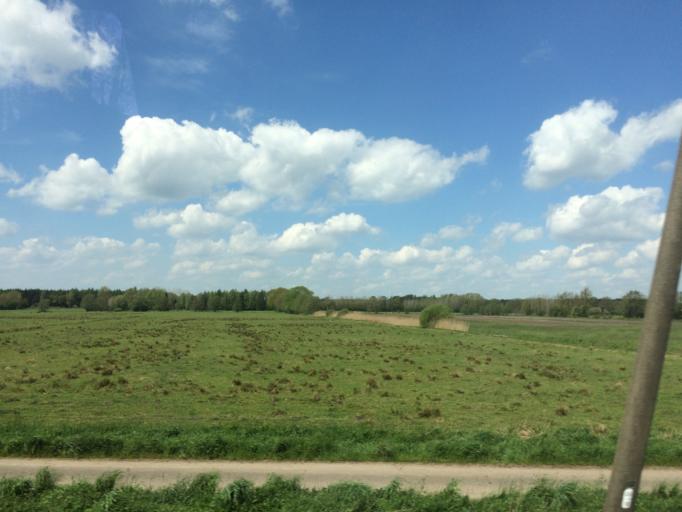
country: DE
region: Schleswig-Holstein
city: Borstel
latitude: 53.9778
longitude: 9.8001
